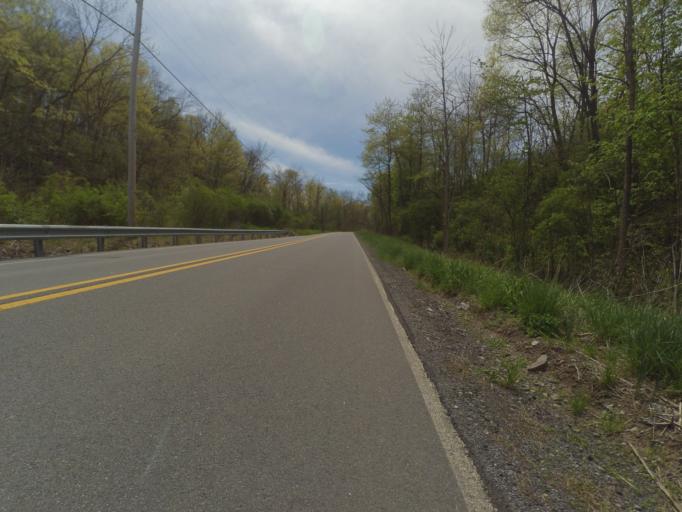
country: US
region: Pennsylvania
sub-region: Blair County
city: Tyrone
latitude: 40.6576
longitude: -78.2207
